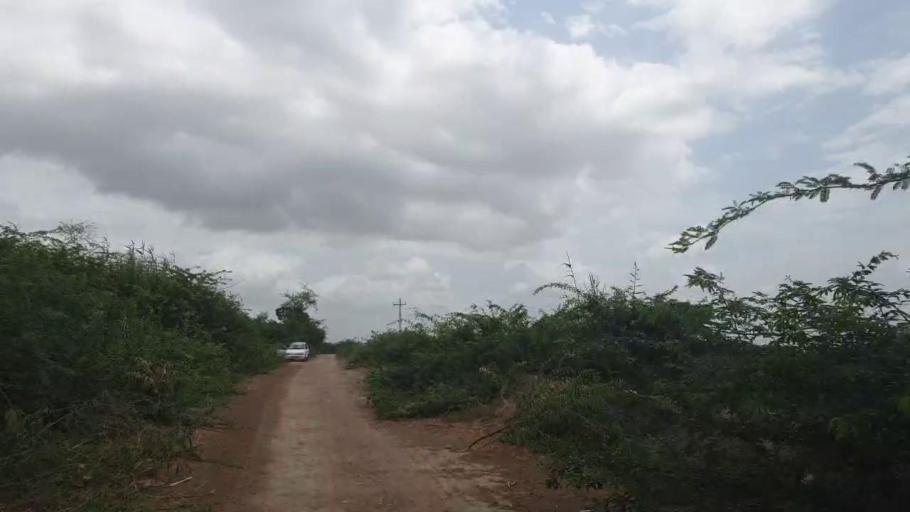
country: PK
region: Sindh
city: Badin
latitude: 24.6331
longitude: 68.9479
